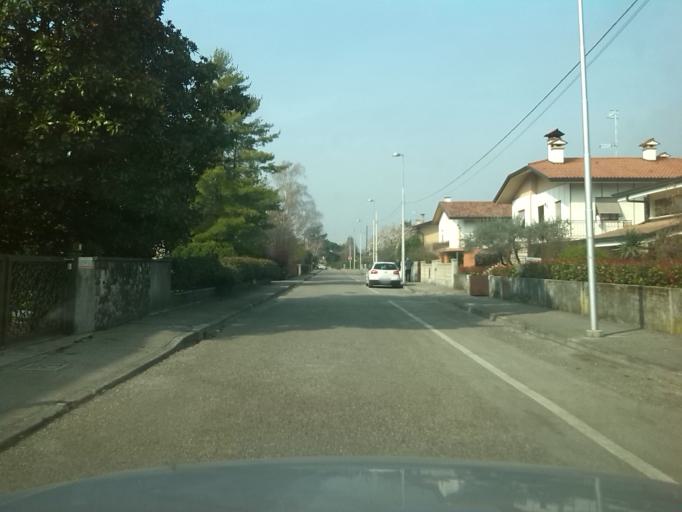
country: IT
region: Friuli Venezia Giulia
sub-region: Provincia di Udine
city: Corno di Rosazzo
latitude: 46.0012
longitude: 13.4387
